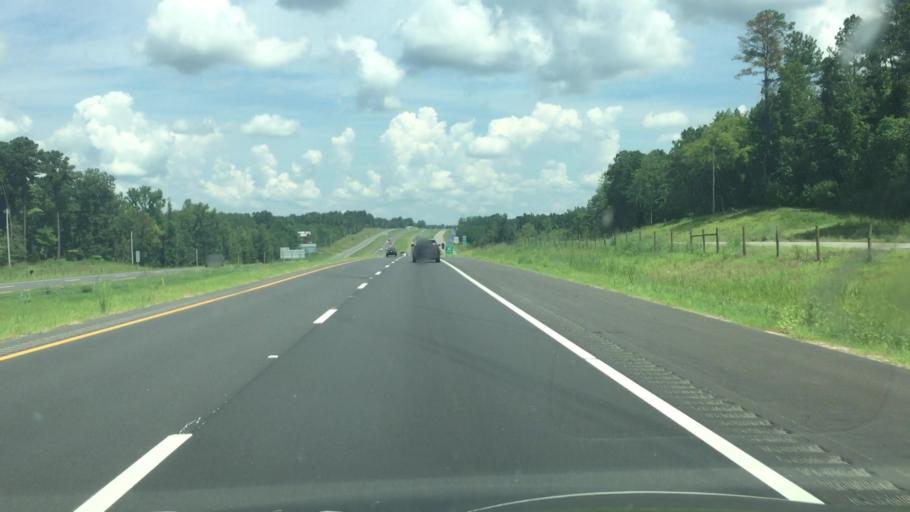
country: US
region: North Carolina
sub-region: Richmond County
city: Ellerbe
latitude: 35.0216
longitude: -79.7698
